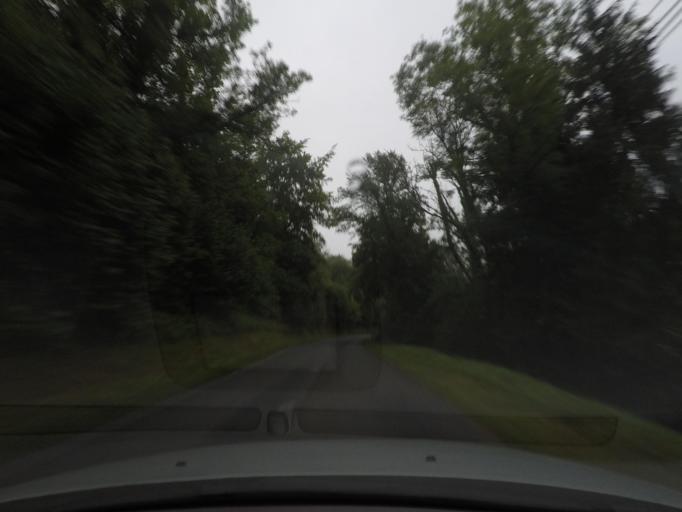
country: FR
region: Haute-Normandie
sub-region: Departement de la Seine-Maritime
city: Fontaine-le-Bourg
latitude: 49.5793
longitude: 1.2149
